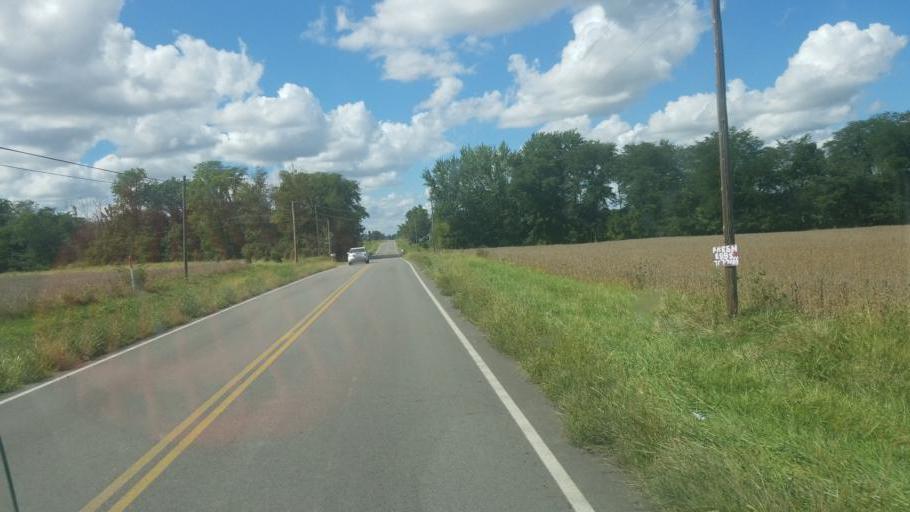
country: US
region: Ohio
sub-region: Union County
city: Marysville
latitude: 40.1830
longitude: -83.4501
